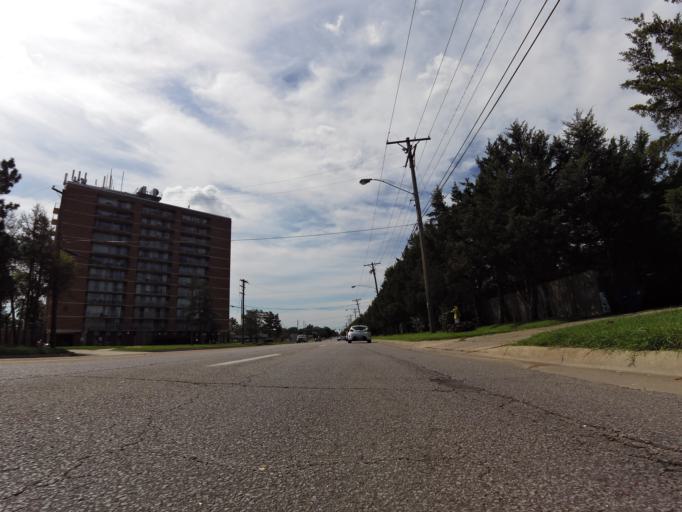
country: US
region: Kansas
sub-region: Sedgwick County
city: Bellaire
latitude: 37.7103
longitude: -97.2623
